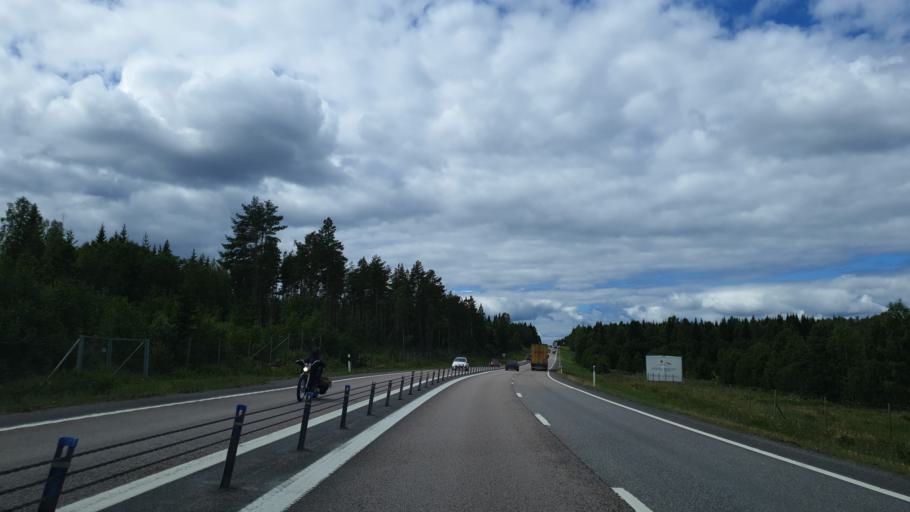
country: SE
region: Vaesternorrland
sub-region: Timra Kommun
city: Soraker
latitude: 62.5346
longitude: 17.5383
